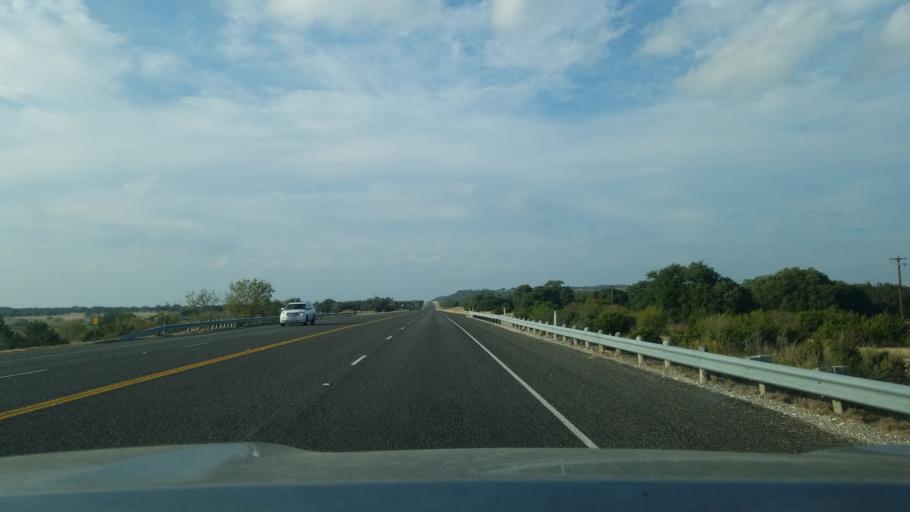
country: US
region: Texas
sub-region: Mills County
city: Goldthwaite
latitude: 31.2437
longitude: -98.4245
